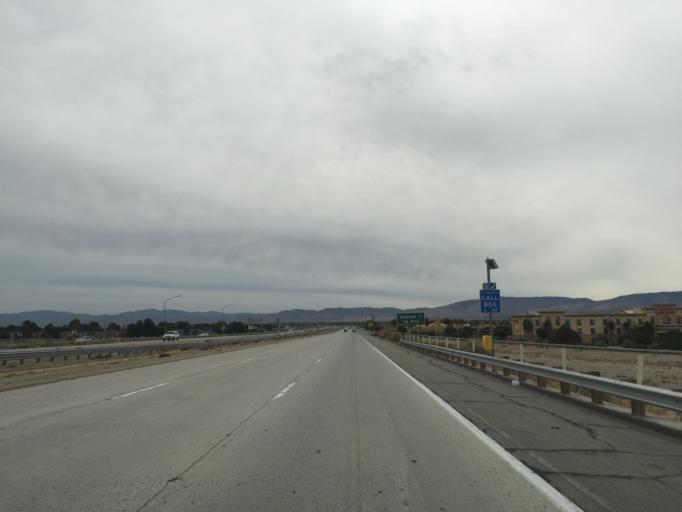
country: US
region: California
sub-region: Los Angeles County
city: Lancaster
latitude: 34.7033
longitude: -118.1703
